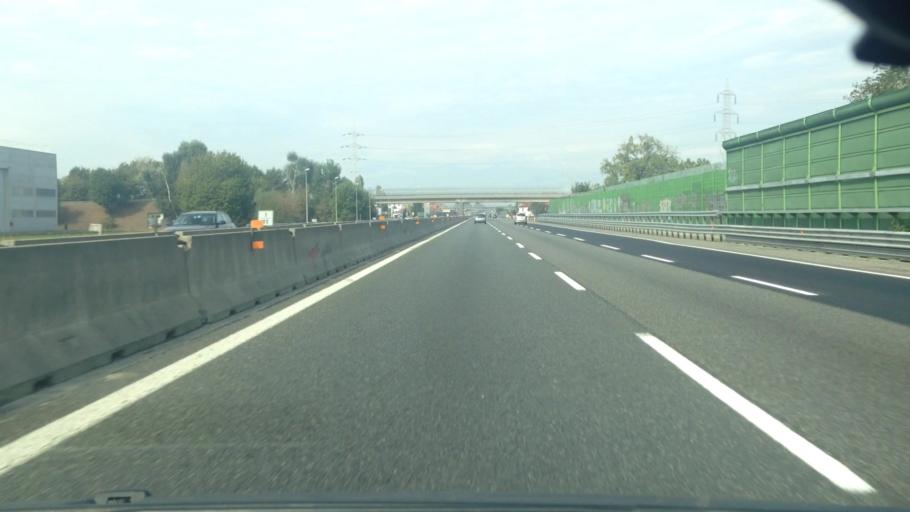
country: IT
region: Piedmont
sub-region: Provincia di Torino
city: Tagliaferro
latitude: 44.9795
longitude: 7.6492
